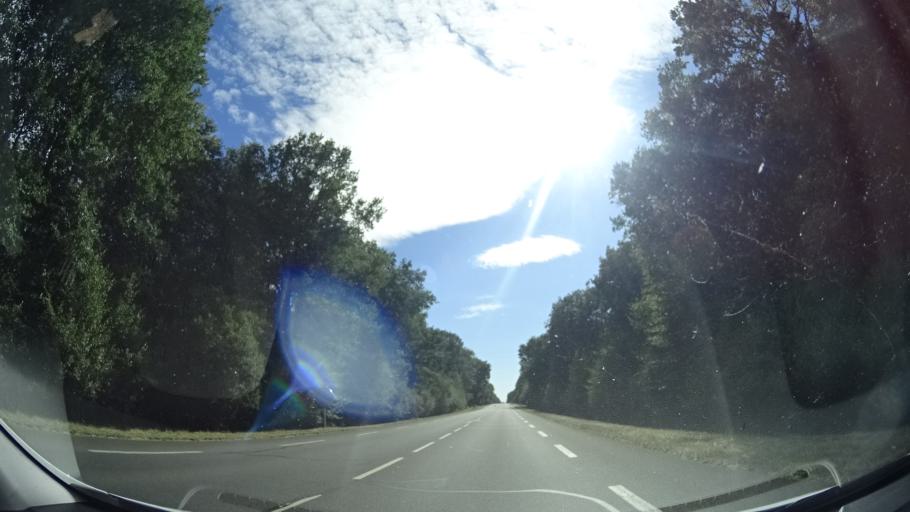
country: FR
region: Centre
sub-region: Departement du Loiret
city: Vitry-aux-Loges
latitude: 47.9294
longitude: 2.3367
